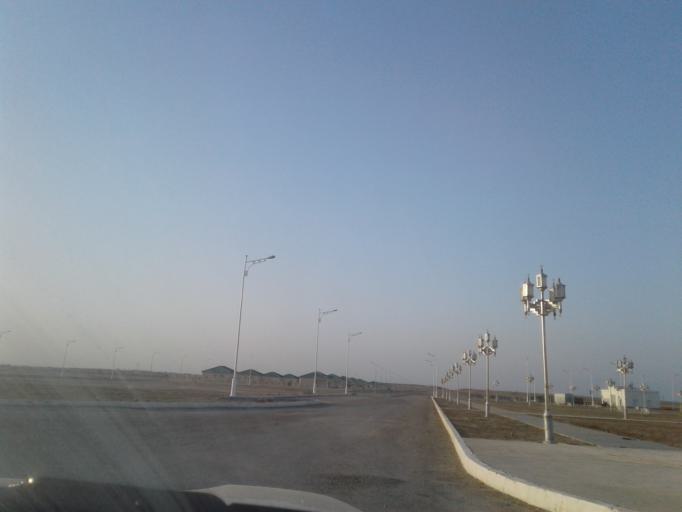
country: IR
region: Golestan
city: Aq Qayeh
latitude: 37.7050
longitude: 54.7419
